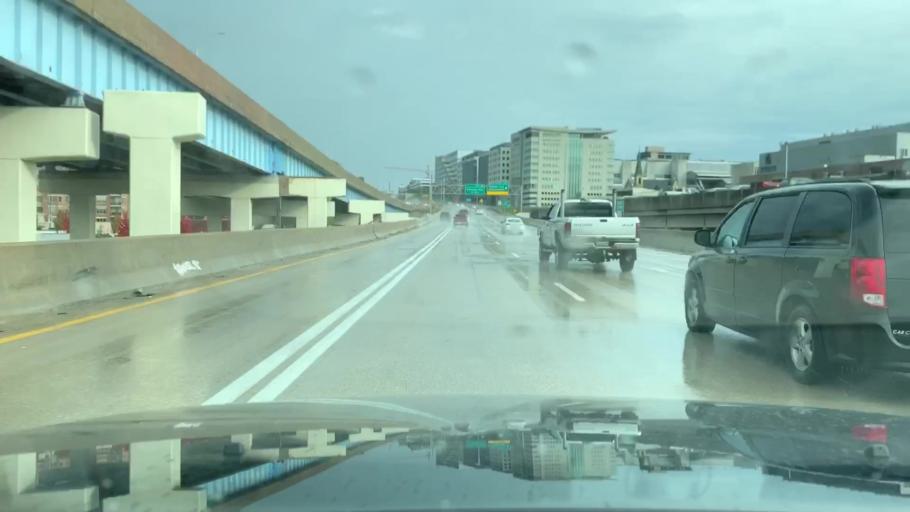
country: US
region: Michigan
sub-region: Kent County
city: Grand Rapids
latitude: 42.9723
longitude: -85.6742
